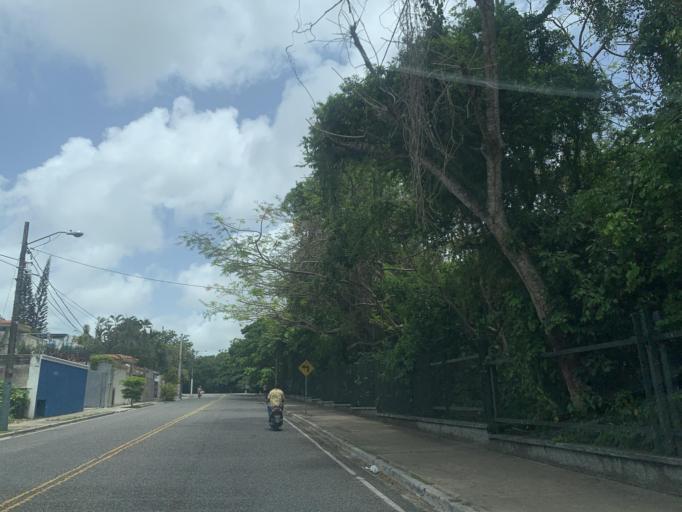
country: DO
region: Nacional
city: La Agustina
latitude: 18.4996
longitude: -69.9474
